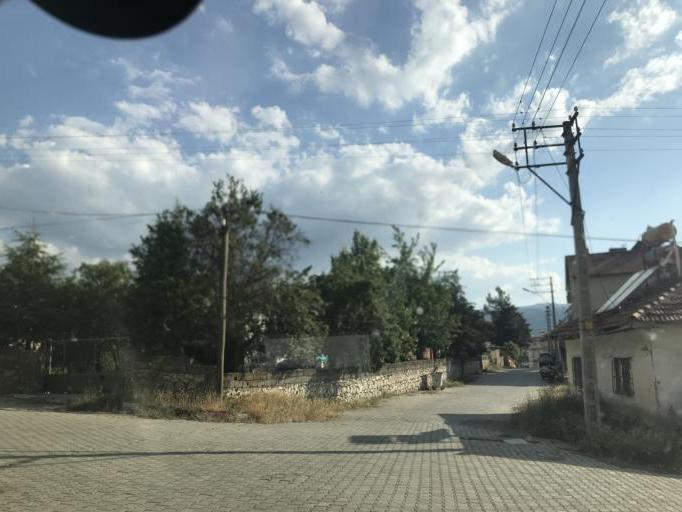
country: TR
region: Burdur
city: Yesilova
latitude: 37.5051
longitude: 29.7566
